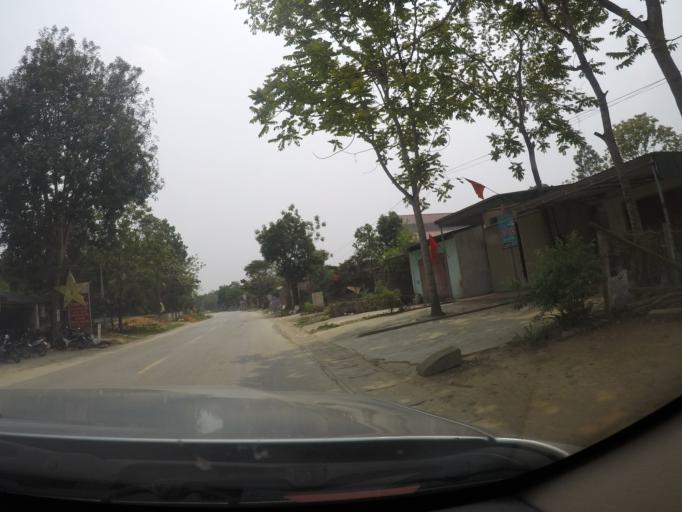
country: VN
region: Thanh Hoa
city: Thi Tran Thuong Xuan
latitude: 19.8011
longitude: 105.3964
